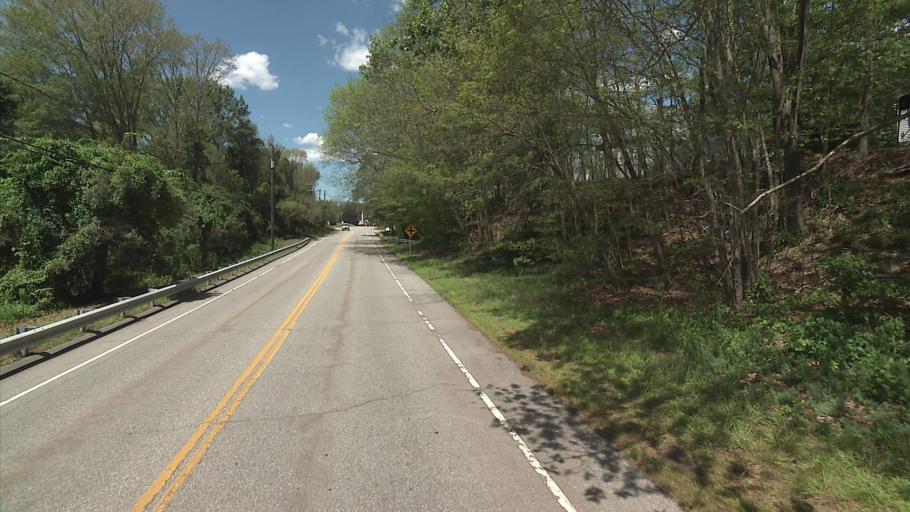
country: US
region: Connecticut
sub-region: Middlesex County
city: Moodus
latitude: 41.4966
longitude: -72.4618
